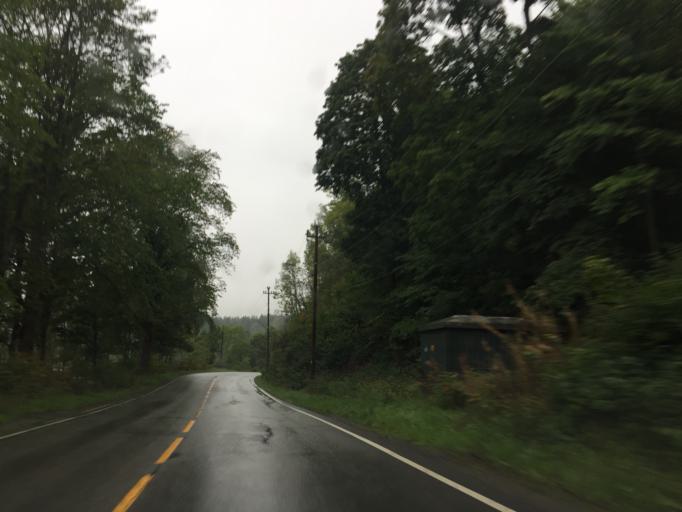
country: NO
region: Akershus
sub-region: Baerum
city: Lysaker
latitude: 59.9663
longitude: 10.6381
